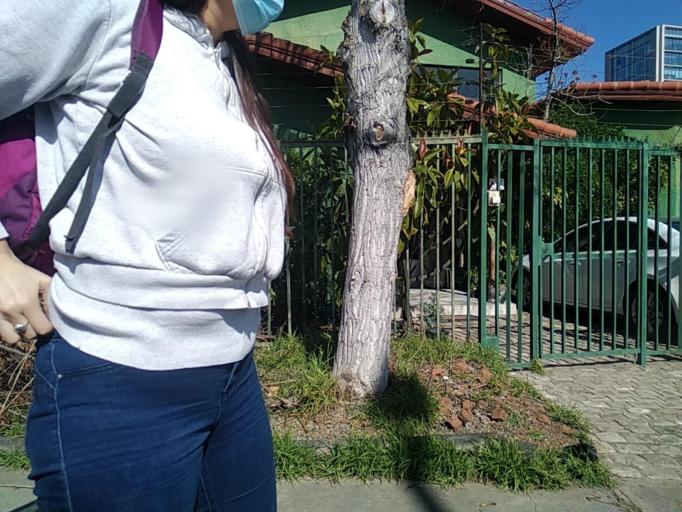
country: CL
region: Valparaiso
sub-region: Provincia de Valparaiso
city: Vina del Mar
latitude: -32.9418
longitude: -71.5448
